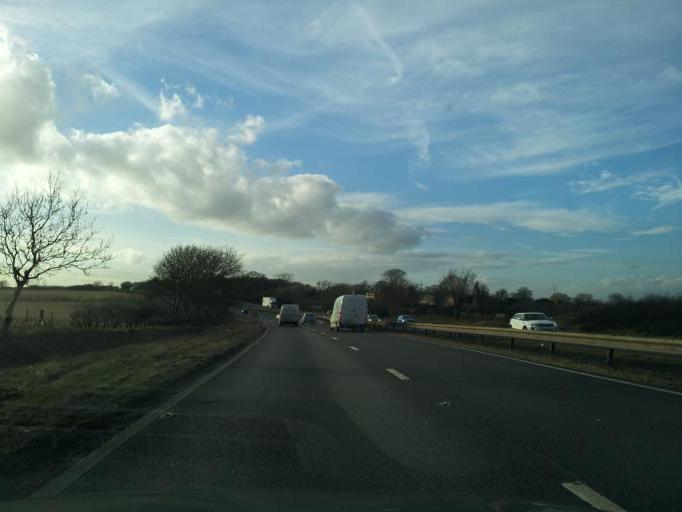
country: GB
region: England
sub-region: Peterborough
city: Castor
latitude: 52.5597
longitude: -0.3599
